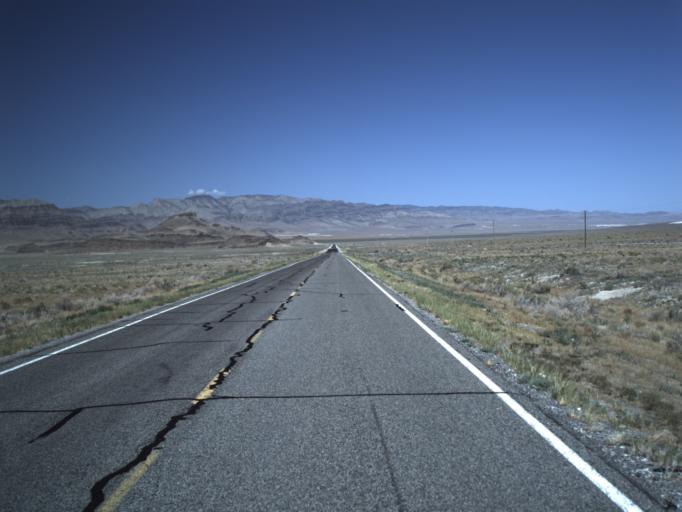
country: US
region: Utah
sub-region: Beaver County
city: Milford
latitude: 39.0448
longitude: -113.4086
